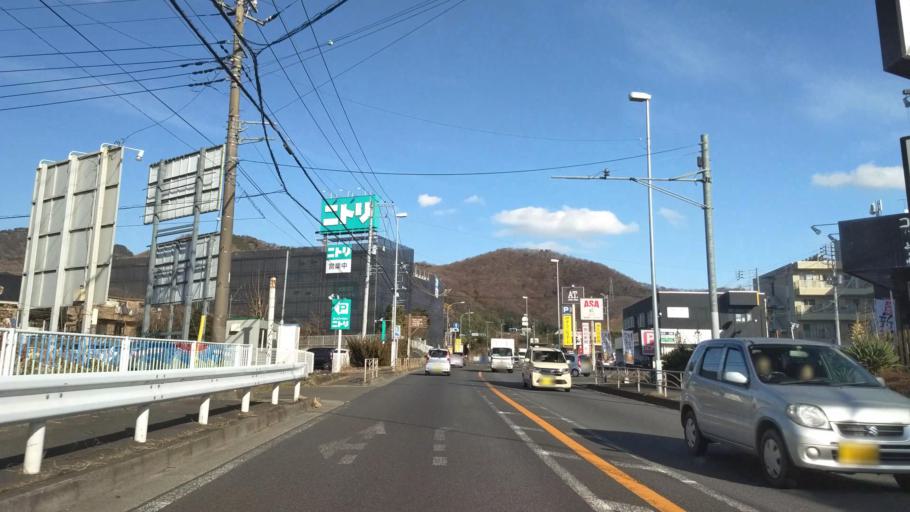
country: JP
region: Kanagawa
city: Hadano
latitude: 35.3824
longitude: 139.2406
